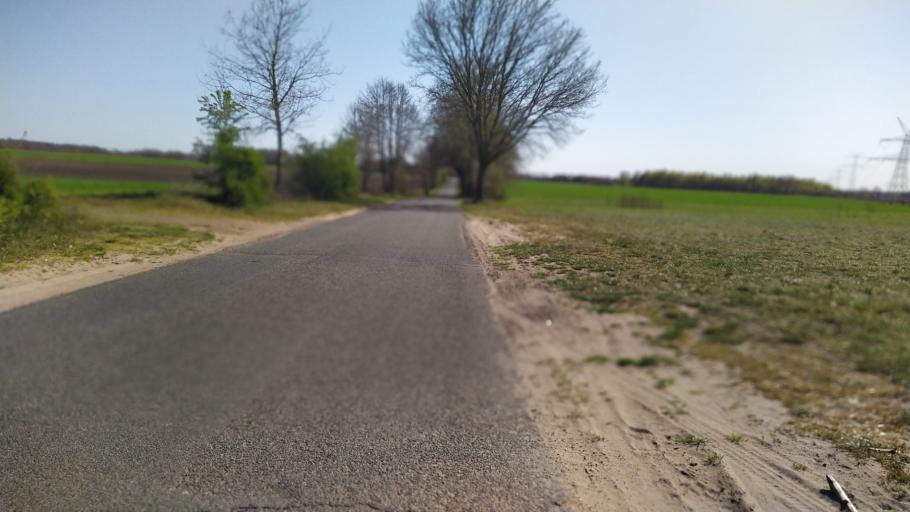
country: DE
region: Lower Saxony
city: Heeslingen
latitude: 53.3172
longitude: 9.3882
